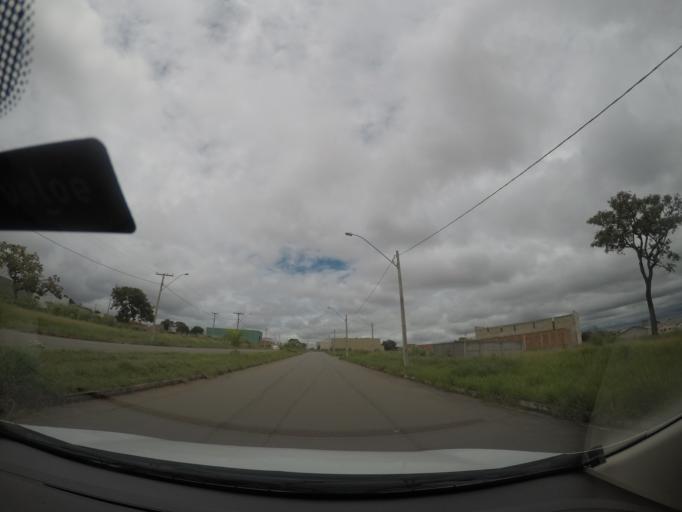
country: BR
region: Goias
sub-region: Goiania
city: Goiania
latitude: -16.7455
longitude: -49.3358
